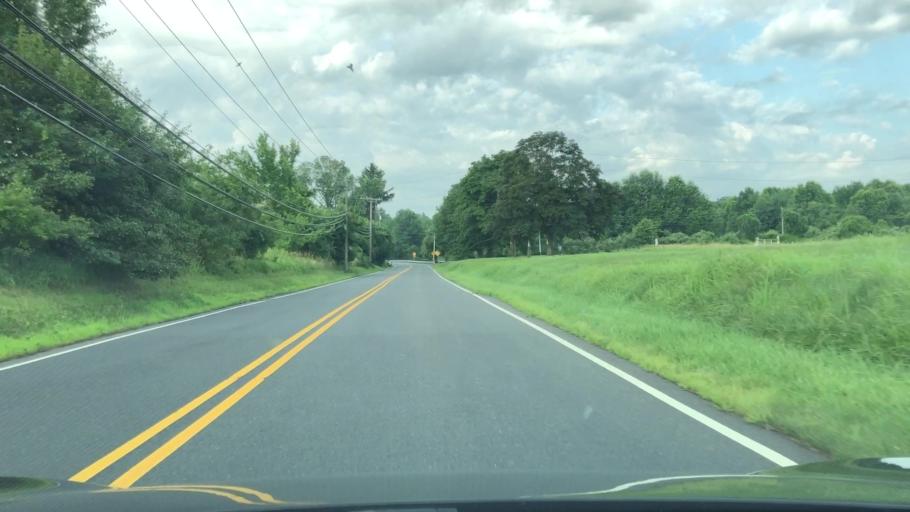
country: US
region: New Jersey
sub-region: Mercer County
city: Pennington
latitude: 40.3341
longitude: -74.7744
